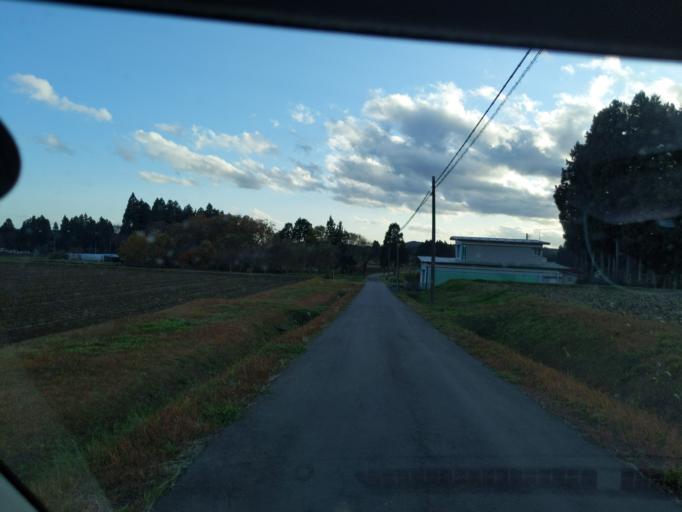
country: JP
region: Iwate
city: Mizusawa
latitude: 39.0879
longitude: 141.0365
